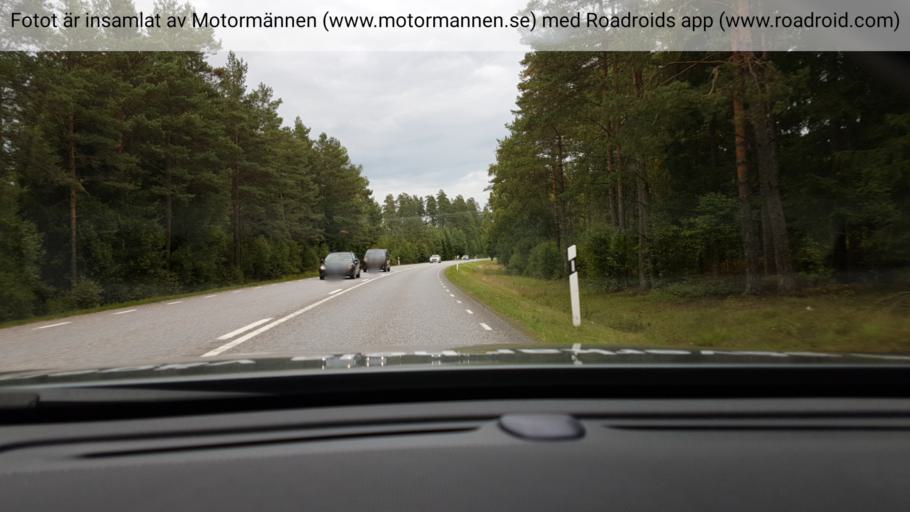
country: SE
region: Joenkoeping
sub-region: Gislaveds Kommun
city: Reftele
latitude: 57.1690
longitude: 13.5736
